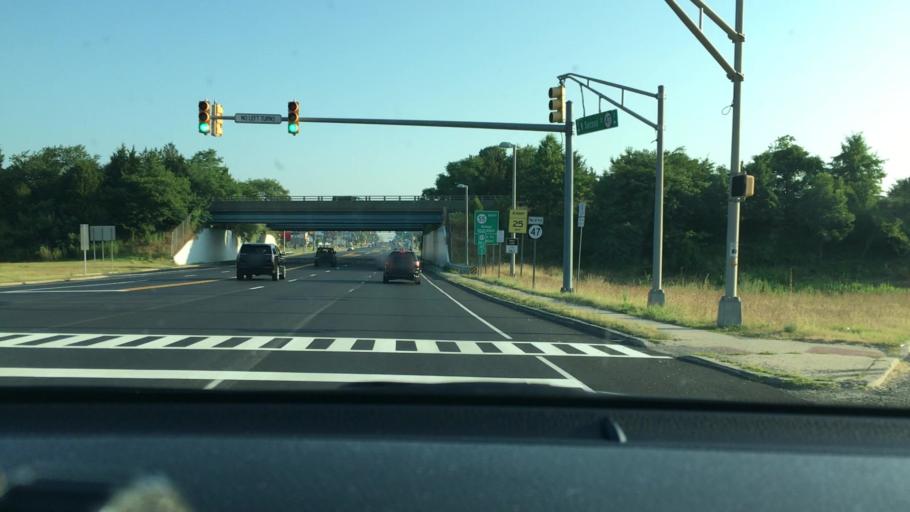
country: US
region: New Jersey
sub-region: Cumberland County
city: South Vineland
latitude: 39.4271
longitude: -75.0399
